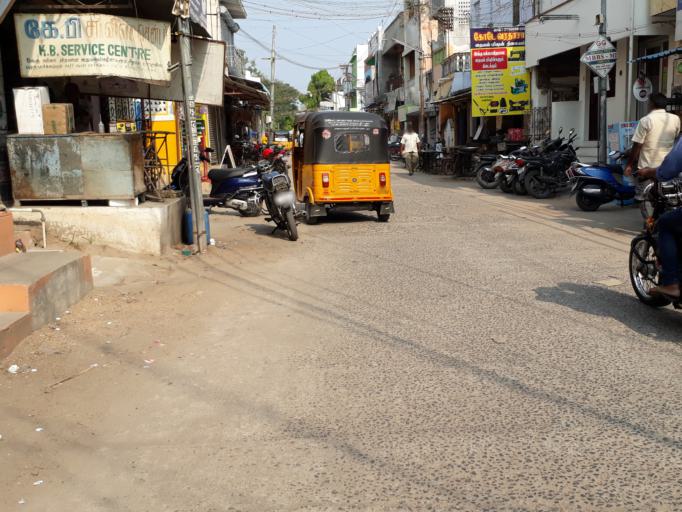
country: IN
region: Tamil Nadu
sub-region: Kancheepuram
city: Kanchipuram
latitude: 12.8321
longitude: 79.7074
